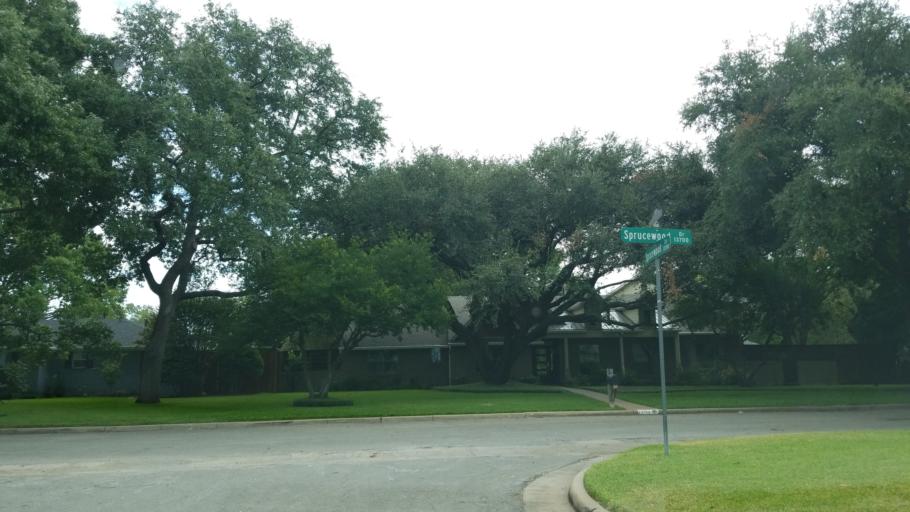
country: US
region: Texas
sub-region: Dallas County
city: Richardson
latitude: 32.9364
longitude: -96.7778
